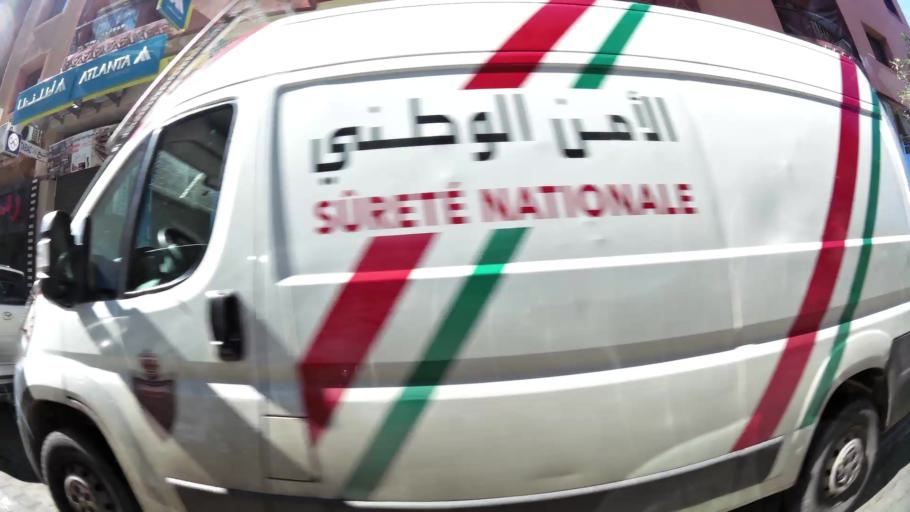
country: MA
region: Marrakech-Tensift-Al Haouz
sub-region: Marrakech
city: Marrakesh
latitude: 31.6348
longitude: -8.0166
